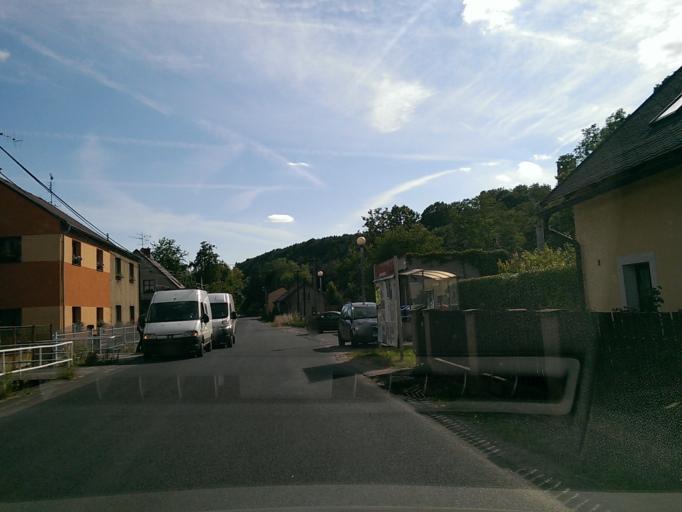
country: CZ
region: Central Bohemia
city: Bakov nad Jizerou
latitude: 50.4697
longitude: 14.9199
